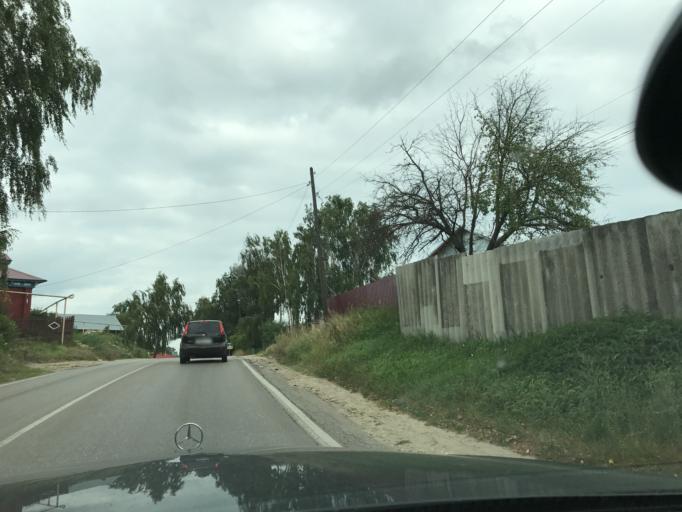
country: RU
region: Nizjnij Novgorod
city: Pavlovo
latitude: 55.9942
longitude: 43.0428
